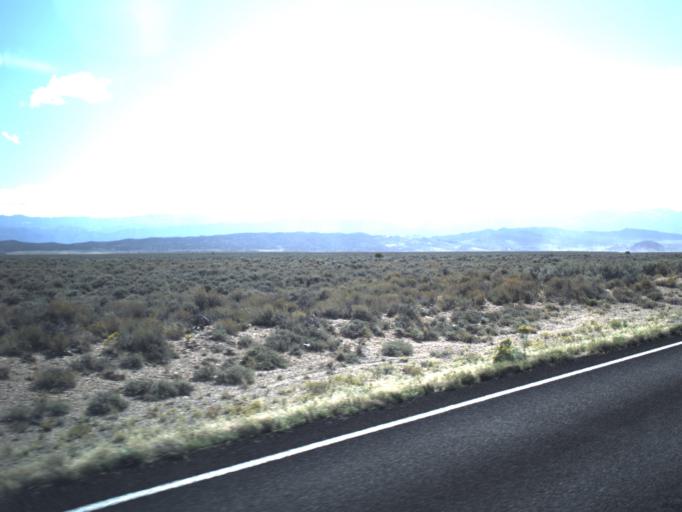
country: US
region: Utah
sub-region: Iron County
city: Enoch
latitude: 37.9937
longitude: -113.0001
